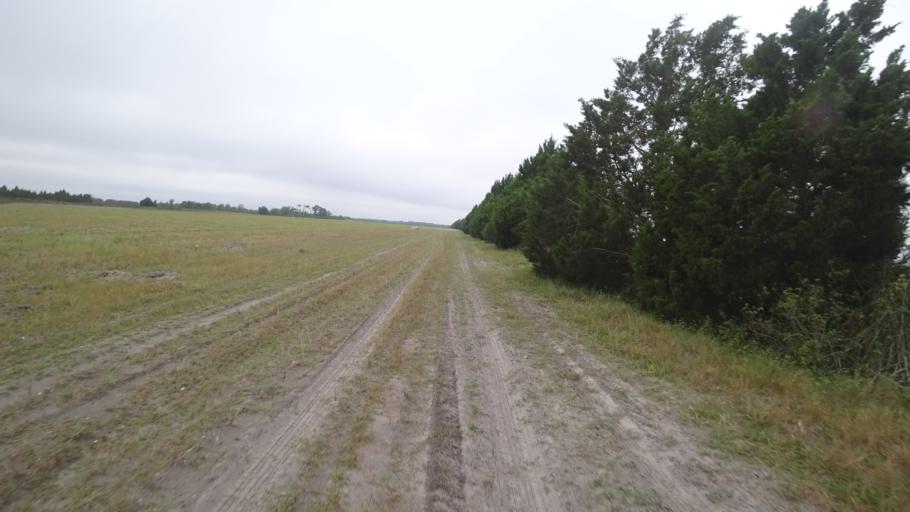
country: US
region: Florida
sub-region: Sarasota County
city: Warm Mineral Springs
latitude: 27.3069
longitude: -82.1497
